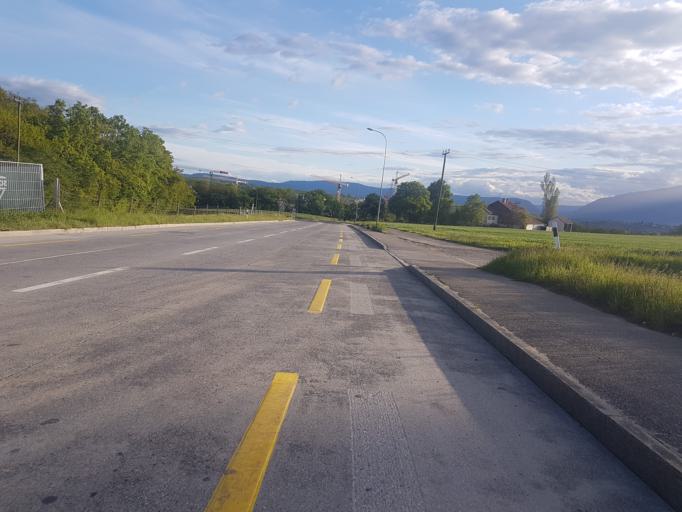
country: CH
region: Geneva
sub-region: Geneva
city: Vernier
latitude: 46.2046
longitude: 6.0641
